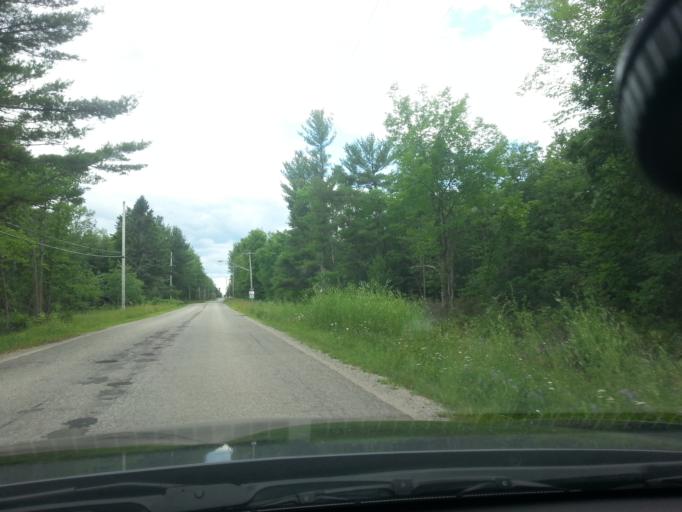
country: CA
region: Ontario
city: Gananoque
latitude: 44.6024
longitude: -76.2293
